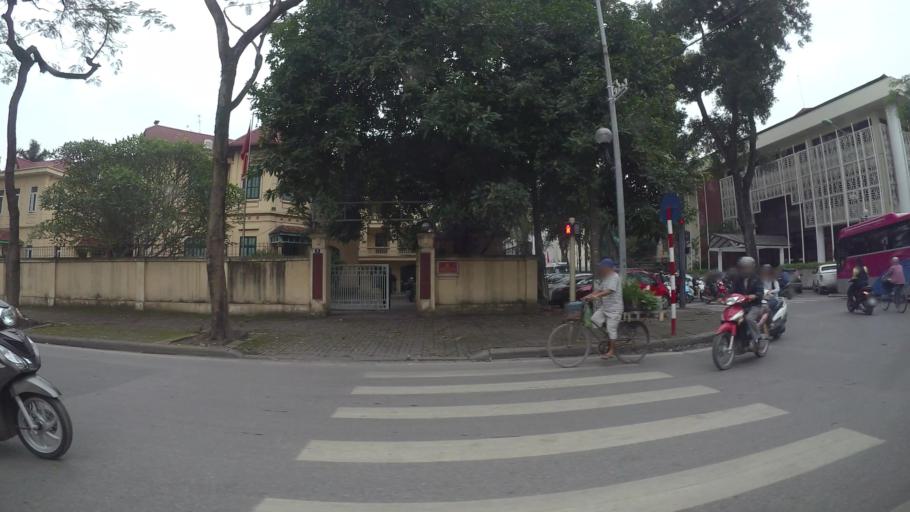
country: VN
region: Ha Noi
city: Hanoi
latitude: 21.0337
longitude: 105.8367
